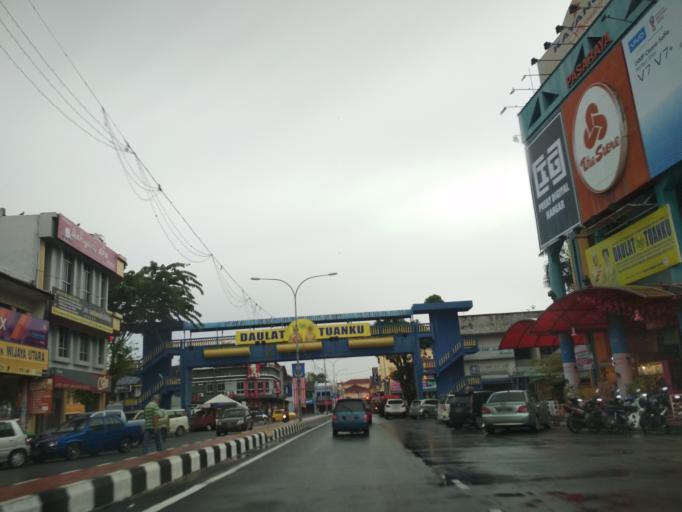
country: MY
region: Perlis
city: Kangar
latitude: 6.4399
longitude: 100.1951
